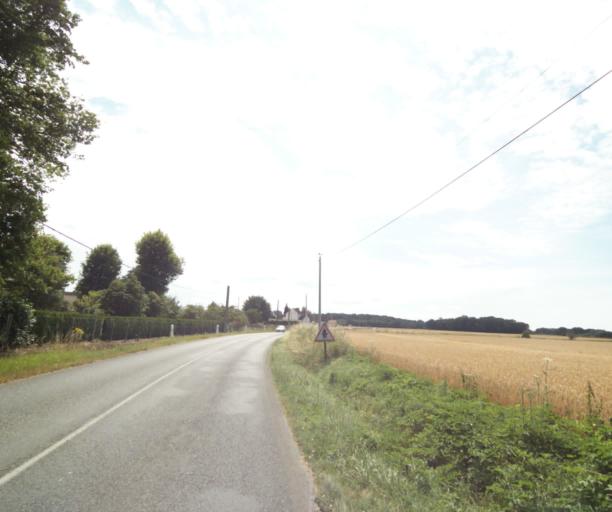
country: FR
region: Ile-de-France
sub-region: Departement de Seine-et-Marne
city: Chailly-en-Biere
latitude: 48.4775
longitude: 2.6219
